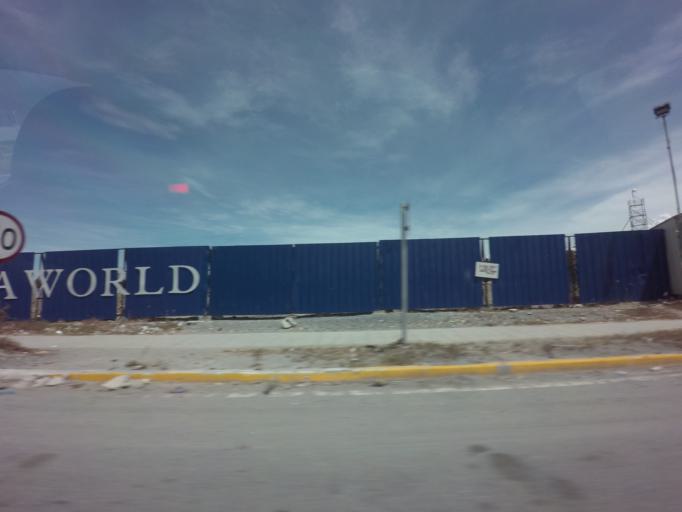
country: PH
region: Metro Manila
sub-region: Makati City
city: Makati City
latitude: 14.5153
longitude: 120.9842
